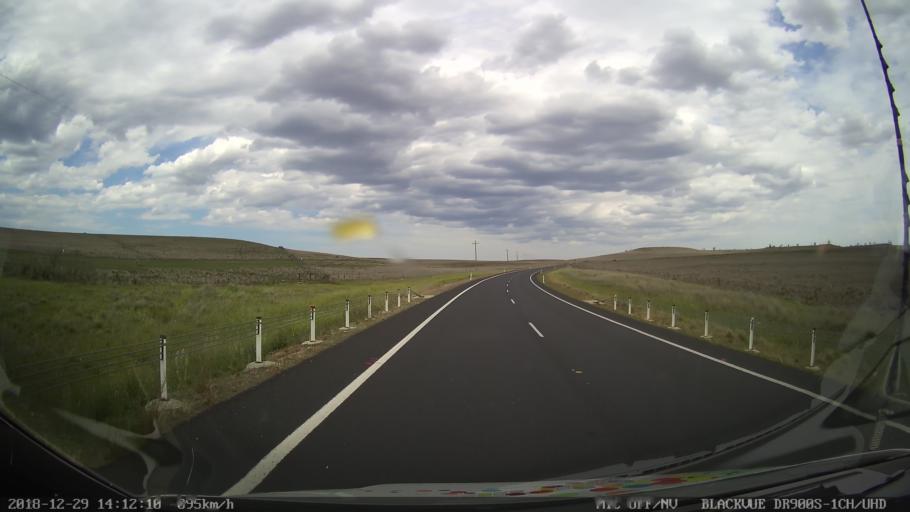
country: AU
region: New South Wales
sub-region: Cooma-Monaro
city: Cooma
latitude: -36.4127
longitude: 149.2293
